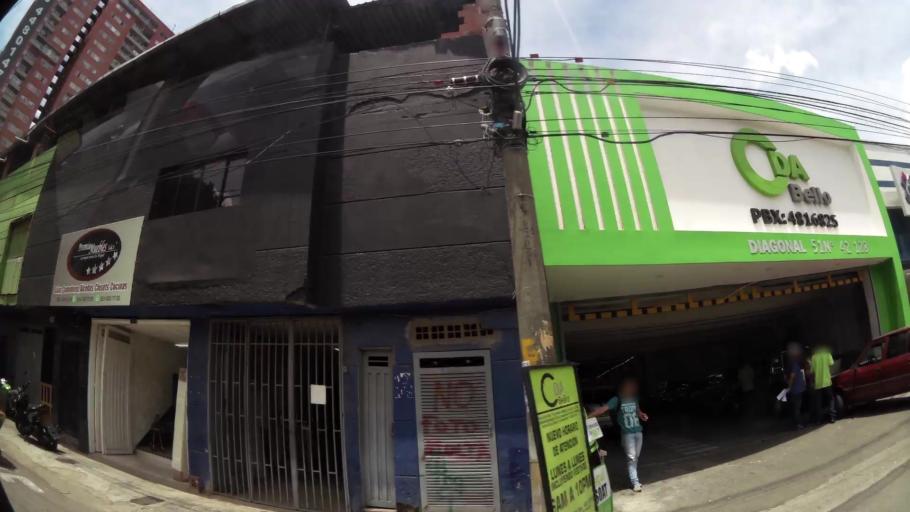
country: CO
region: Antioquia
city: Bello
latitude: 6.3366
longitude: -75.5490
